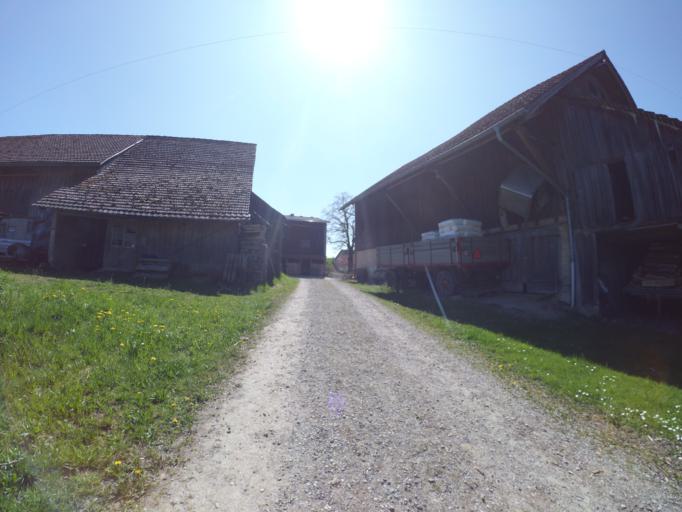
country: CH
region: Thurgau
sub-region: Frauenfeld District
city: Huttwilen
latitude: 47.5966
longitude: 8.8933
